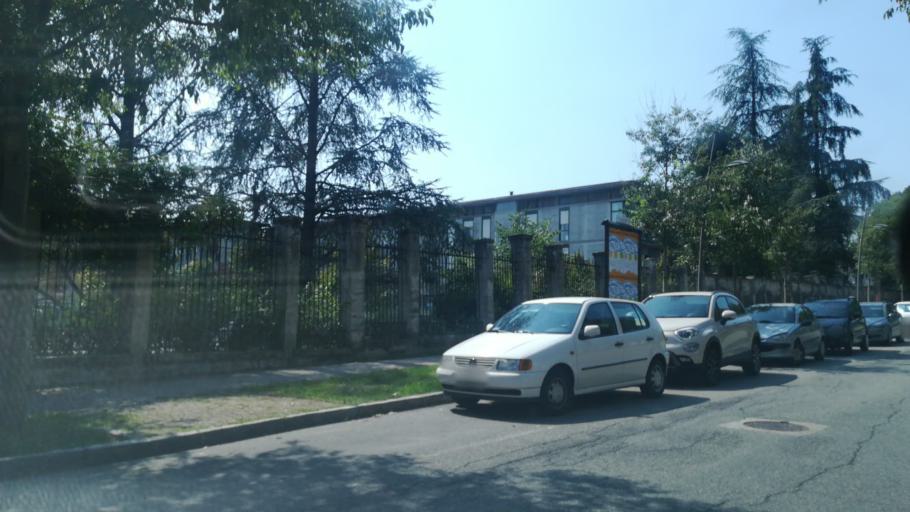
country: IT
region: Piedmont
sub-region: Provincia di Alessandria
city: Casale Monferrato
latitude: 45.1218
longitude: 8.4461
